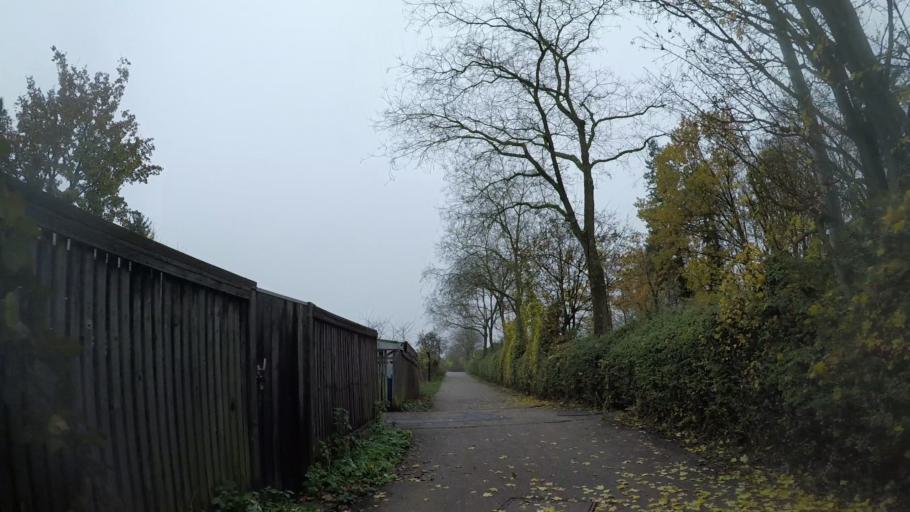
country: DE
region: Baden-Wuerttemberg
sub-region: Tuebingen Region
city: Reutlingen
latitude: 48.5181
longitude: 9.2176
